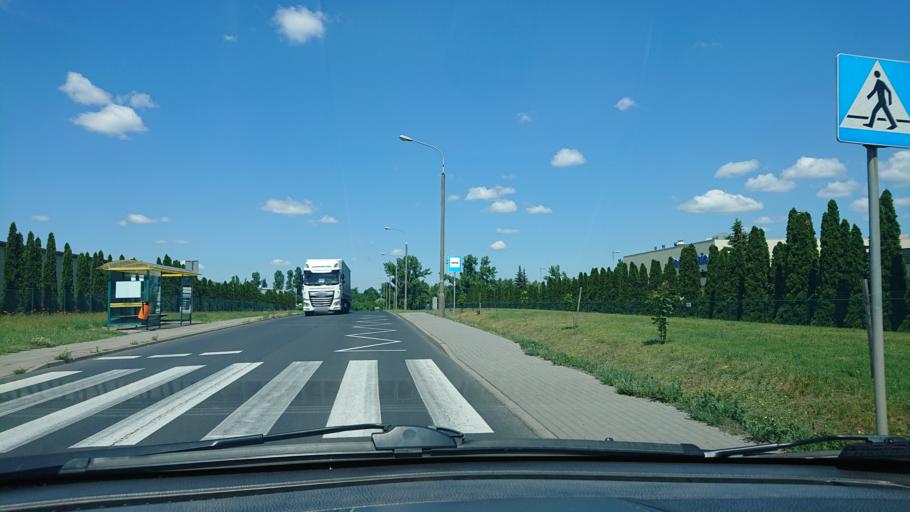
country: PL
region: Greater Poland Voivodeship
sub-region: Powiat gnieznienski
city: Gniezno
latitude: 52.5266
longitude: 17.6185
